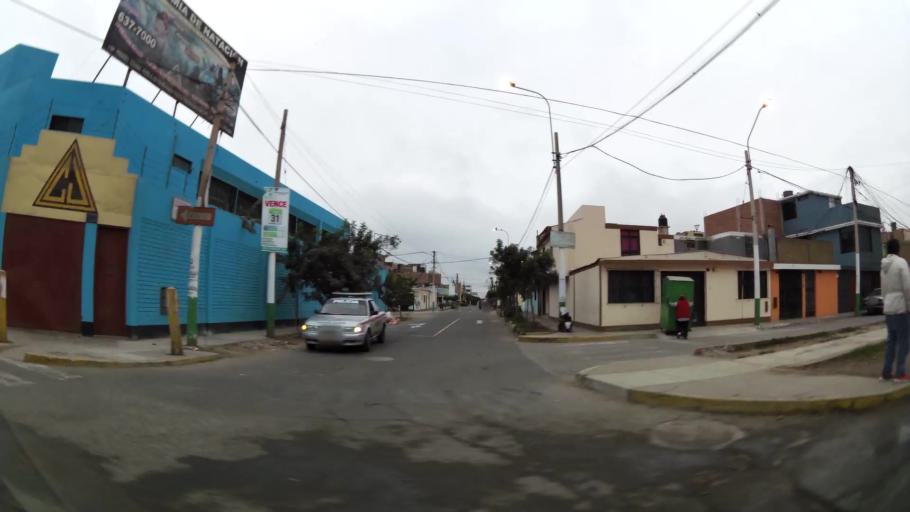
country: PE
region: Callao
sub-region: Callao
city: Callao
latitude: -12.0732
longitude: -77.1215
